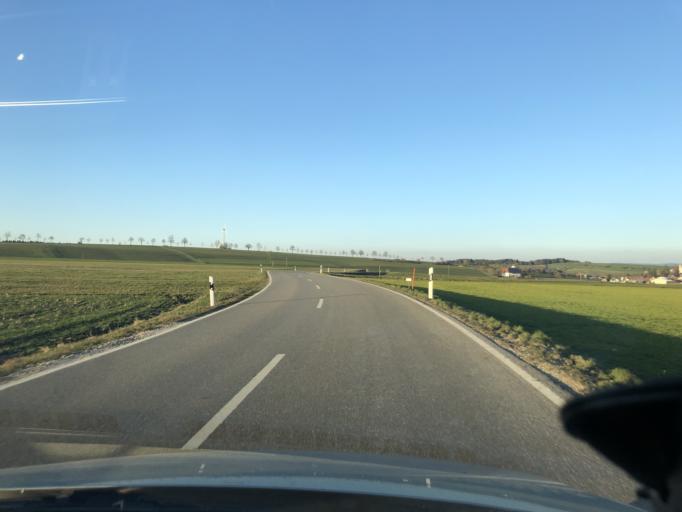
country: DE
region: Baden-Wuerttemberg
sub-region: Freiburg Region
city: Hufingen
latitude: 47.8843
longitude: 8.4747
